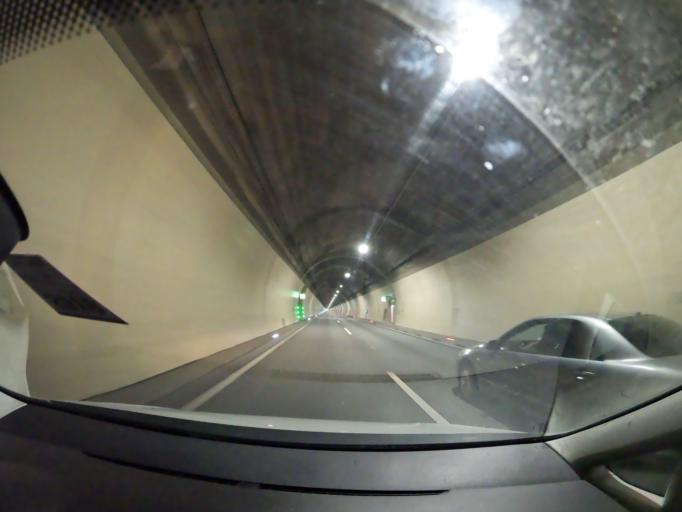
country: AT
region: Carinthia
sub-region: Politischer Bezirk Wolfsberg
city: Bad Sankt Leonhard im Lavanttal
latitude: 46.9044
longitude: 14.8215
